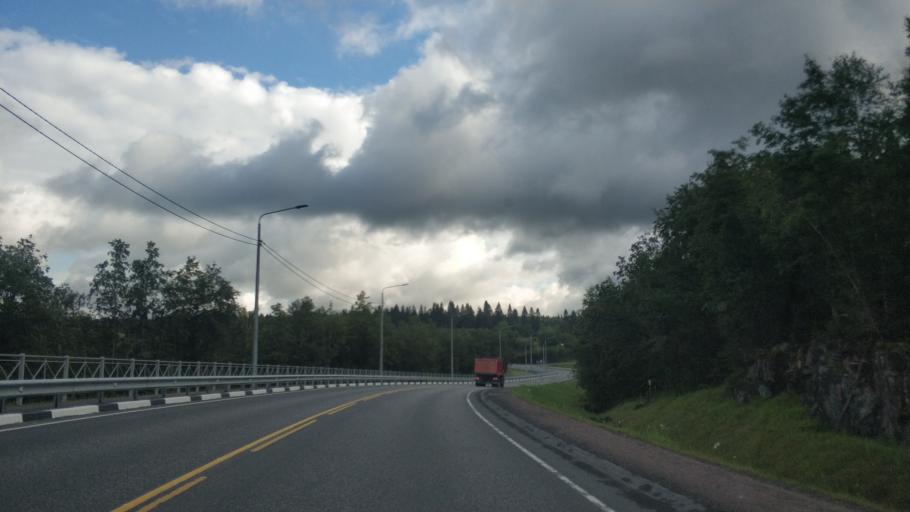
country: RU
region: Republic of Karelia
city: Ruskeala
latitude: 61.9437
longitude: 30.5947
